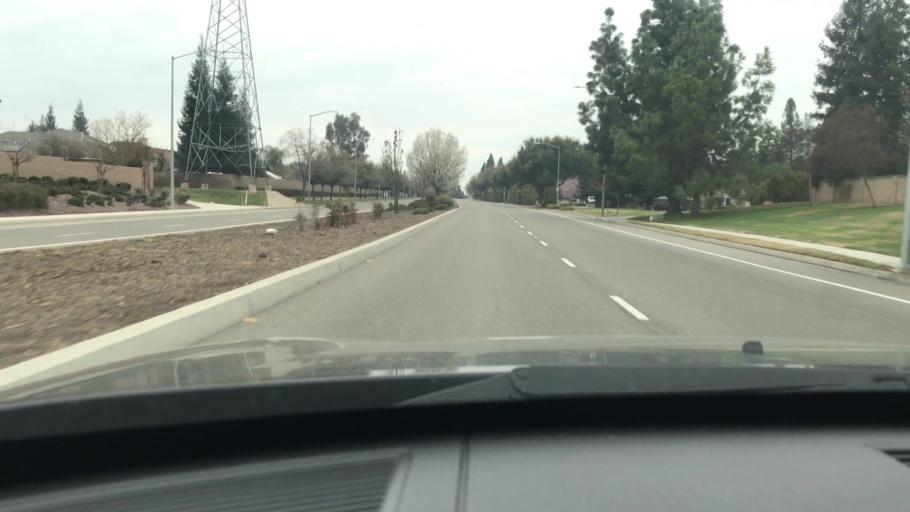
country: US
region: California
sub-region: Fresno County
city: Clovis
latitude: 36.8271
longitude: -119.6640
